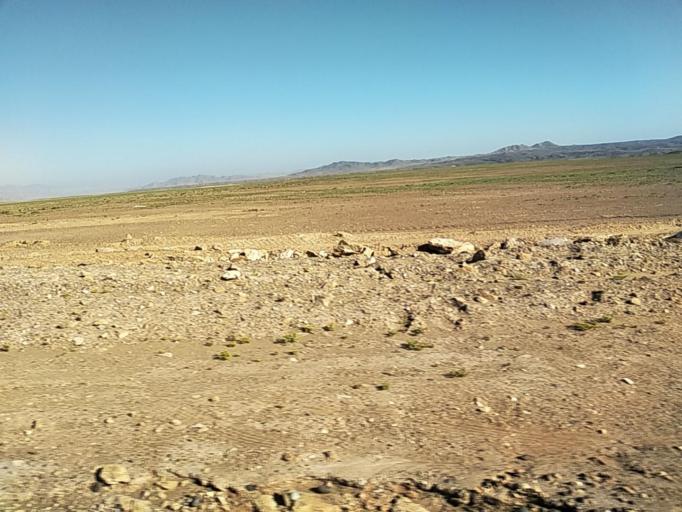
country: CL
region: Atacama
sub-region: Provincia de Copiapo
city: Copiapo
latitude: -27.3222
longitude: -70.7527
